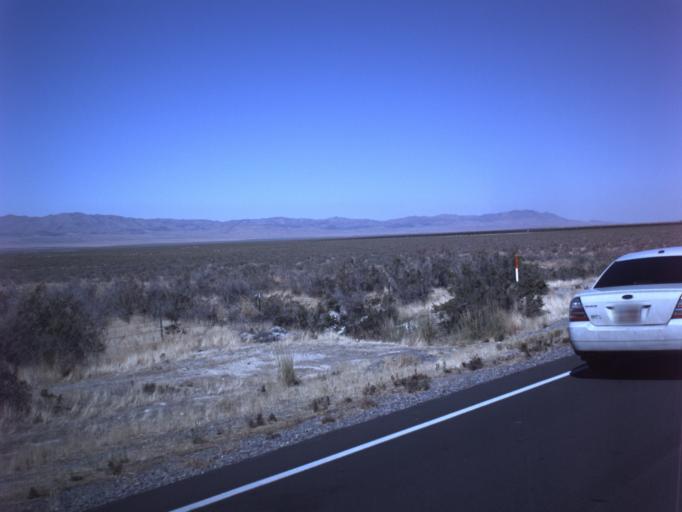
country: US
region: Utah
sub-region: Tooele County
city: Grantsville
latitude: 40.4747
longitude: -112.7460
